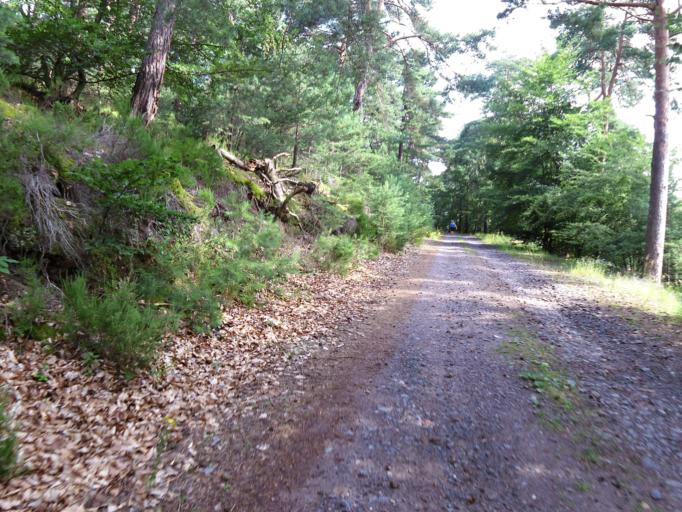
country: DE
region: Rheinland-Pfalz
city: Bad Duerkheim
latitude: 49.4478
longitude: 8.1260
